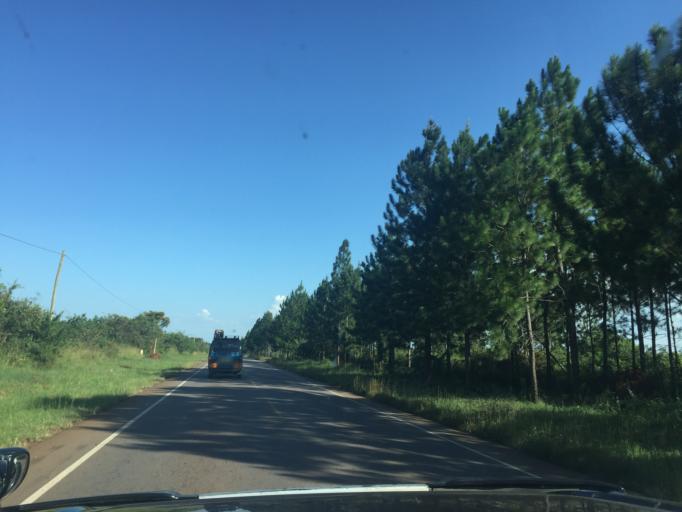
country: UG
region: Central Region
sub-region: Nakasongola District
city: Nakasongola
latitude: 1.3832
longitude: 32.3349
